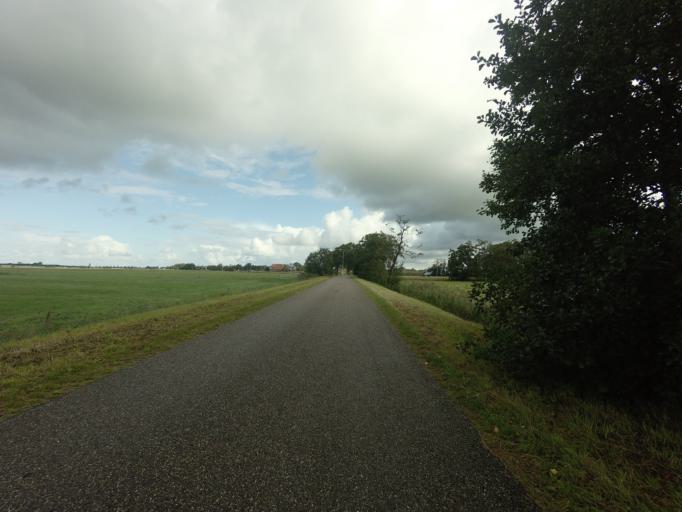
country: NL
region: Friesland
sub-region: Gemeente Tytsjerksteradiel
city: Garyp
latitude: 53.1536
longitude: 5.9505
